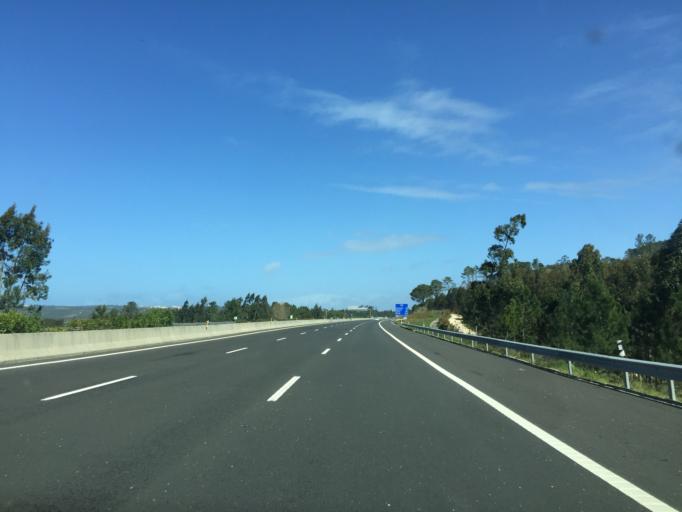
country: PT
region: Leiria
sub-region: Nazare
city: Nazare
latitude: 39.5110
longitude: -9.0889
